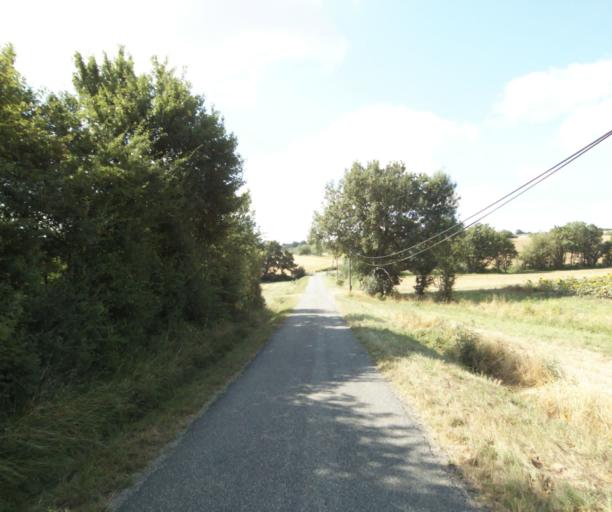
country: FR
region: Midi-Pyrenees
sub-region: Departement de la Haute-Garonne
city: Saint-Felix-Lauragais
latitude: 43.4492
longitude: 1.8284
